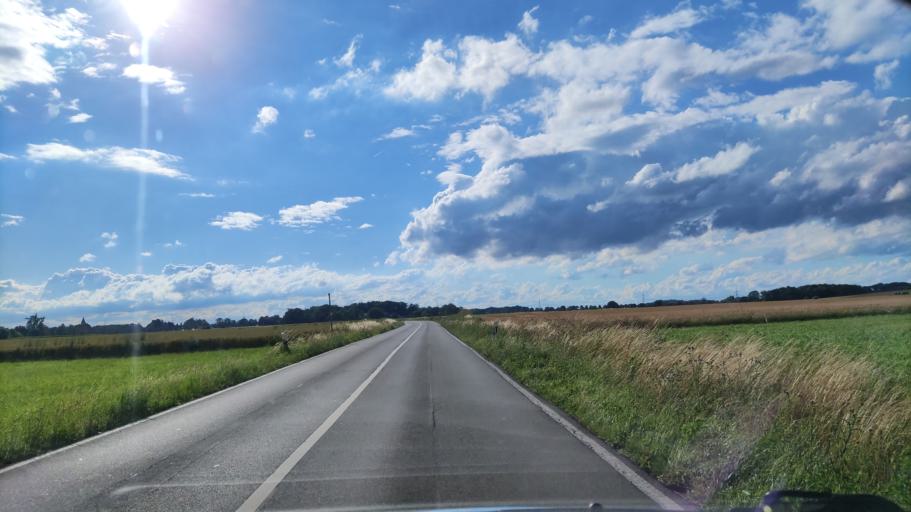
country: DE
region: North Rhine-Westphalia
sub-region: Regierungsbezirk Arnsberg
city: Welver
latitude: 51.6415
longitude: 7.9844
